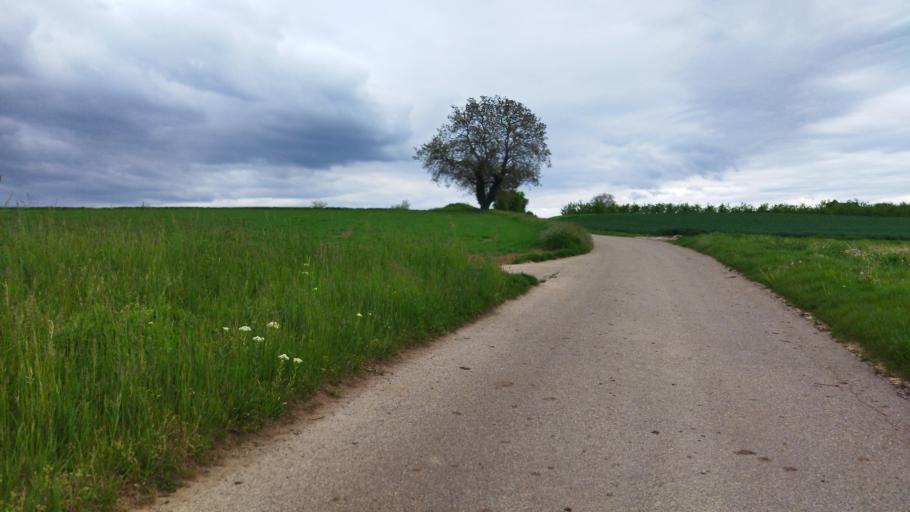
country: DE
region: Baden-Wuerttemberg
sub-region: Regierungsbezirk Stuttgart
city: Lauffen am Neckar
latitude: 49.0860
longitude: 9.1586
